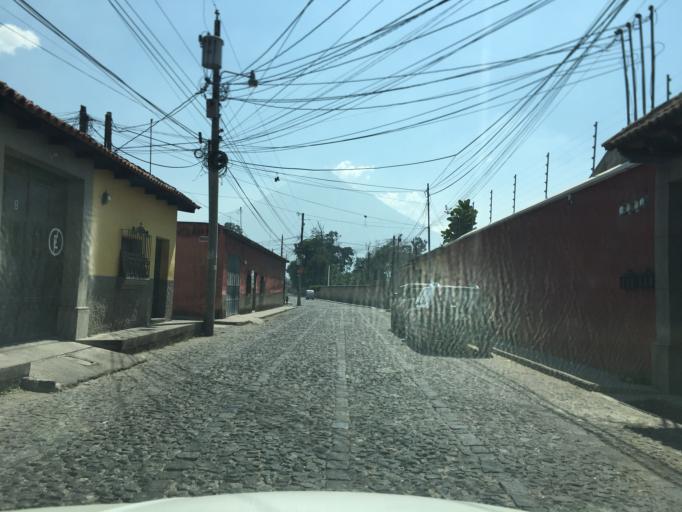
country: GT
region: Sacatepequez
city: Antigua Guatemala
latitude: 14.5634
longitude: -90.7394
